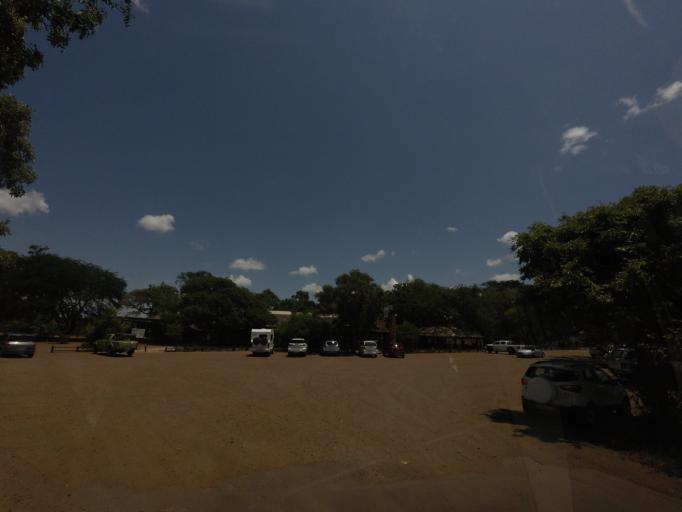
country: ZA
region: Mpumalanga
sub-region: Ehlanzeni District
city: Komatipoort
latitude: -24.7865
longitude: 31.8593
